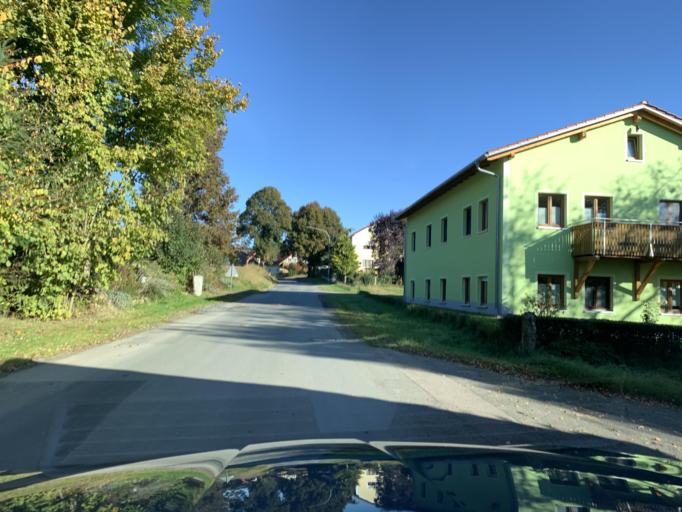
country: DE
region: Bavaria
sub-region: Upper Palatinate
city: Thanstein
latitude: 49.4033
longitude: 12.4634
